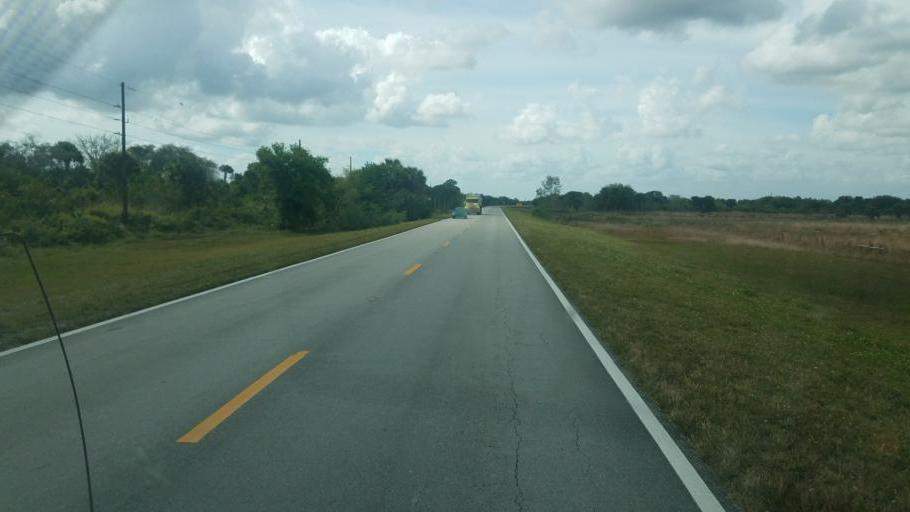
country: US
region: Florida
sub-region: Okeechobee County
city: Cypress Quarters
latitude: 27.4486
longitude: -80.6753
